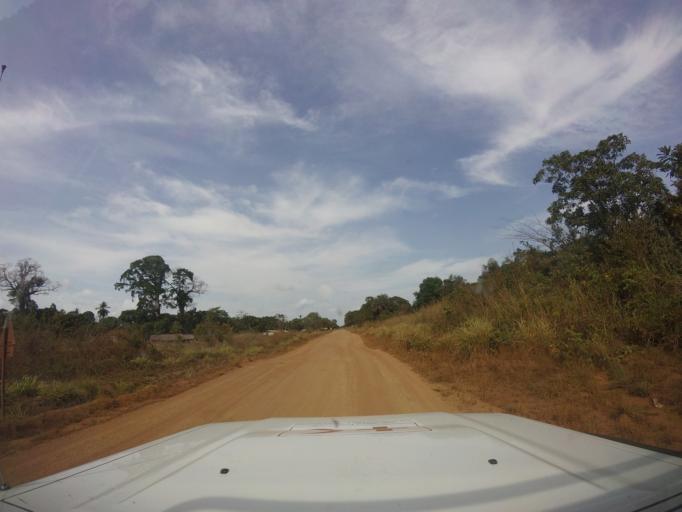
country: LR
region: Grand Cape Mount
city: Robertsport
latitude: 6.6863
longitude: -11.1217
